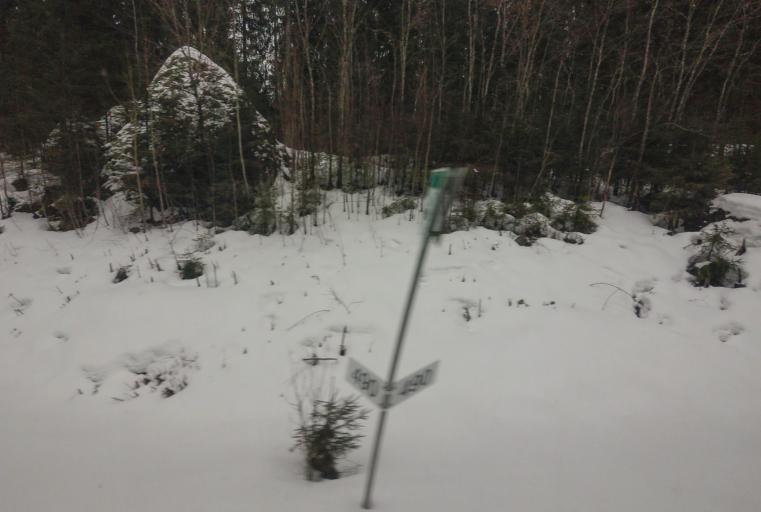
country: FI
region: Southern Savonia
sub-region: Savonlinna
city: Savonlinna
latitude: 61.8636
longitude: 29.0177
